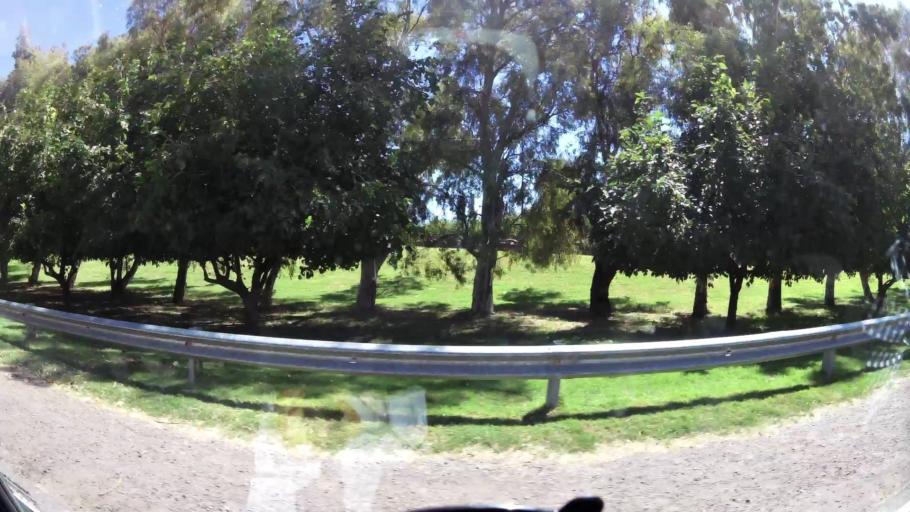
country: AR
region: San Juan
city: San Juan
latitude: -31.5187
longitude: -68.5321
